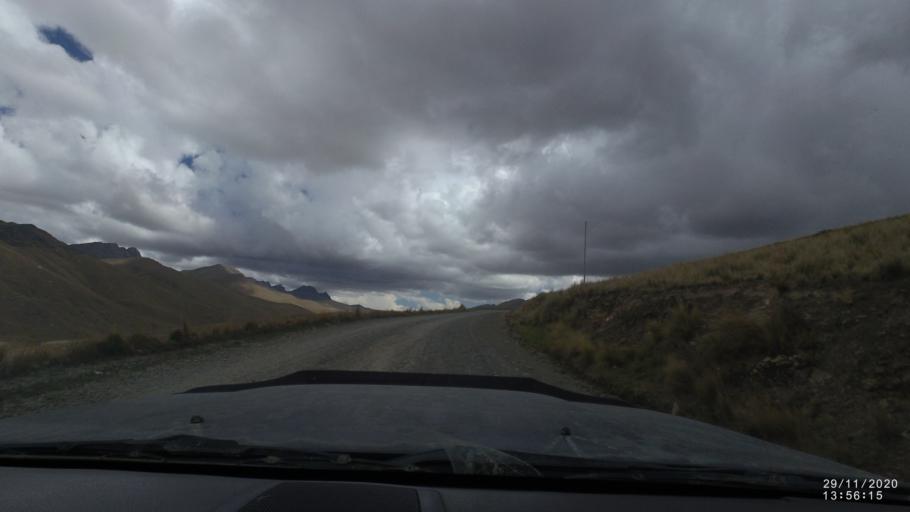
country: BO
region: Cochabamba
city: Sipe Sipe
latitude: -17.1750
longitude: -66.3593
